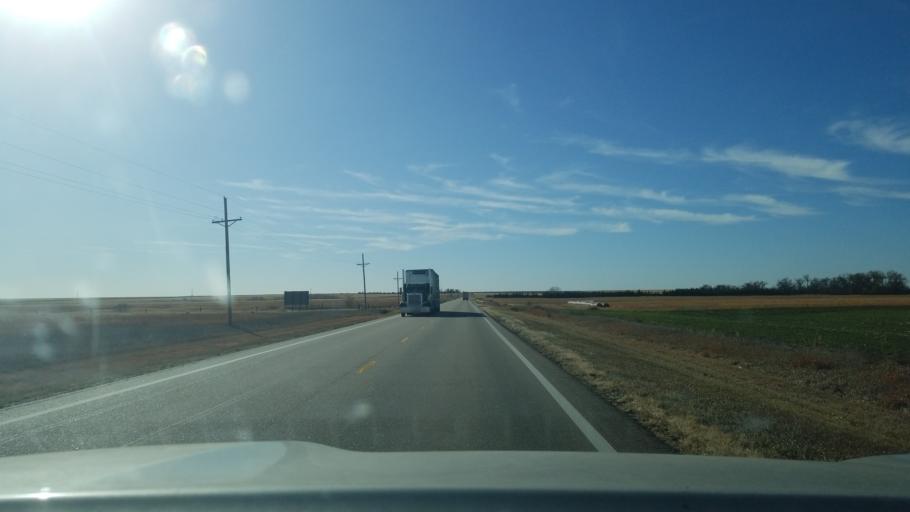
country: US
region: Kansas
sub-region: Ness County
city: Ness City
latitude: 38.4174
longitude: -99.8986
